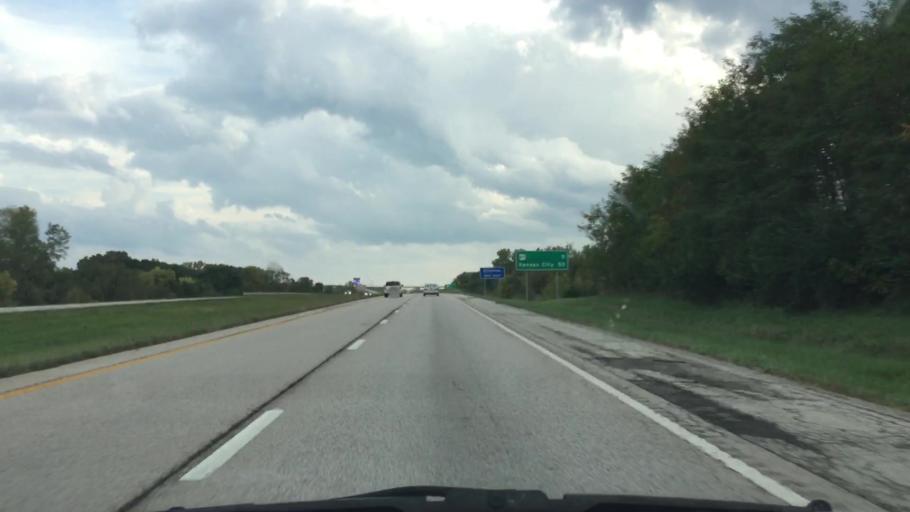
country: US
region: Missouri
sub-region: Clinton County
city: Cameron
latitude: 39.7412
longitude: -94.2204
